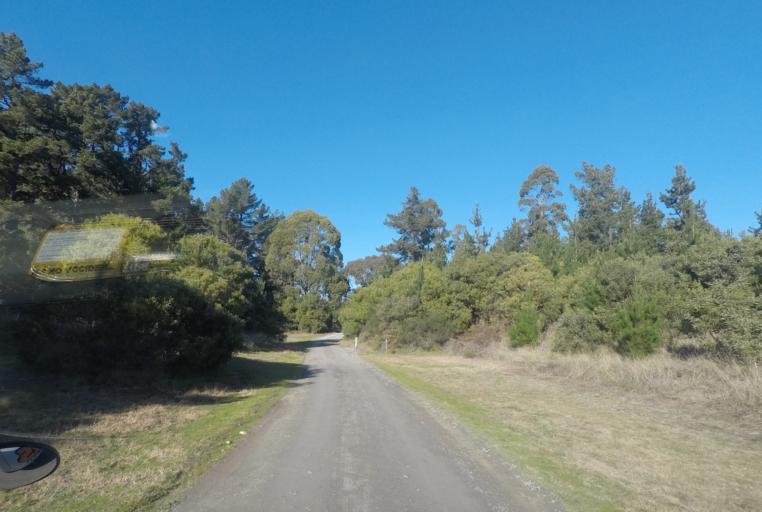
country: NZ
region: Tasman
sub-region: Tasman District
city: Mapua
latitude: -41.2636
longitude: 173.1425
